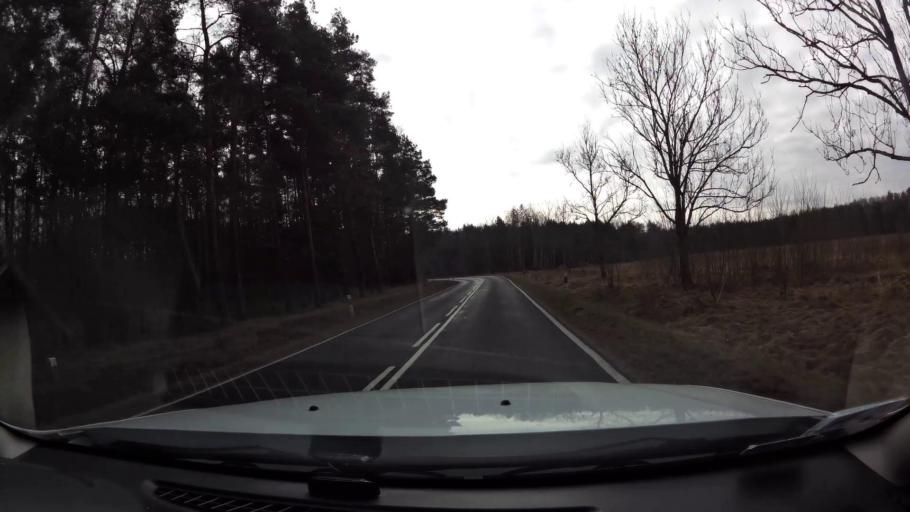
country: PL
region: West Pomeranian Voivodeship
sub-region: Powiat mysliborski
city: Debno
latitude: 52.7602
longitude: 14.6807
